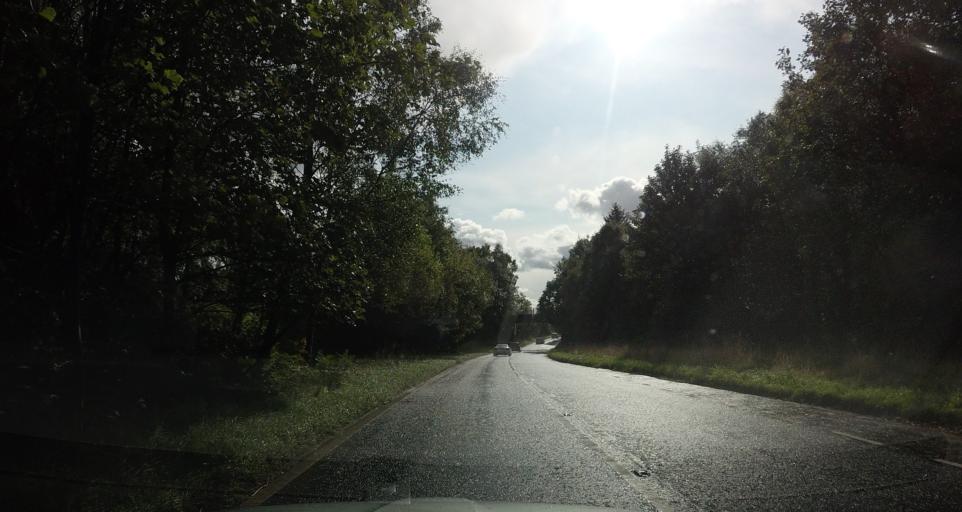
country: GB
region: Scotland
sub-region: Clackmannanshire
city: Clackmannan
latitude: 56.1114
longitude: -3.7076
